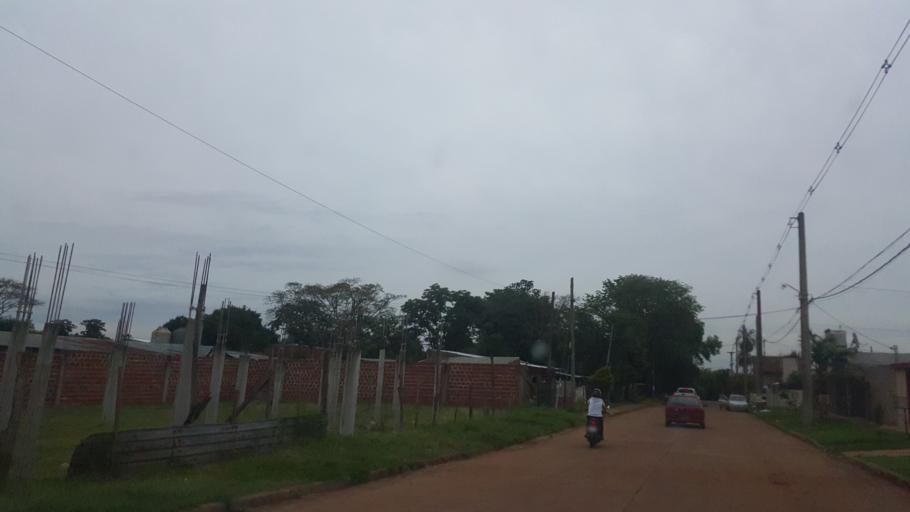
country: AR
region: Misiones
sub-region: Departamento de Capital
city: Posadas
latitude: -27.3600
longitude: -55.9365
